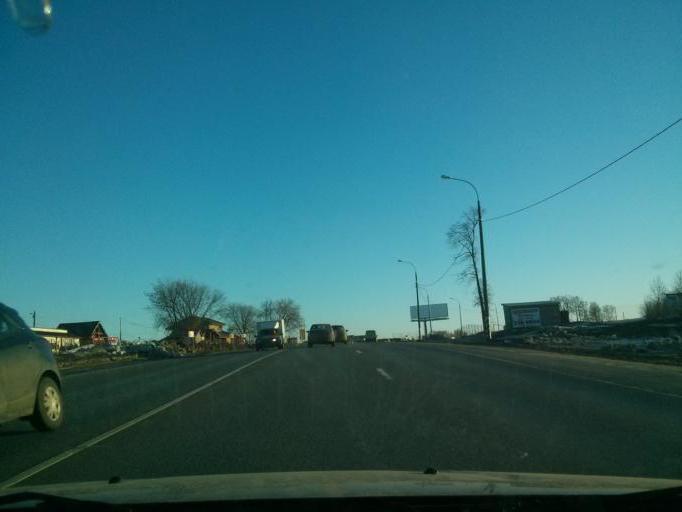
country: RU
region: Nizjnij Novgorod
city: Afonino
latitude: 56.2322
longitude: 44.0985
